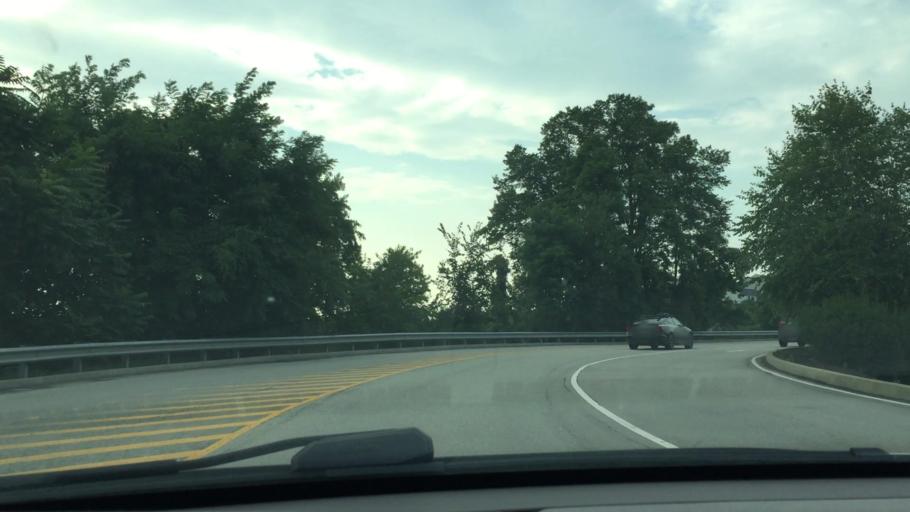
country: US
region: Pennsylvania
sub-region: Washington County
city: McGovern
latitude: 40.2199
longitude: -80.2034
